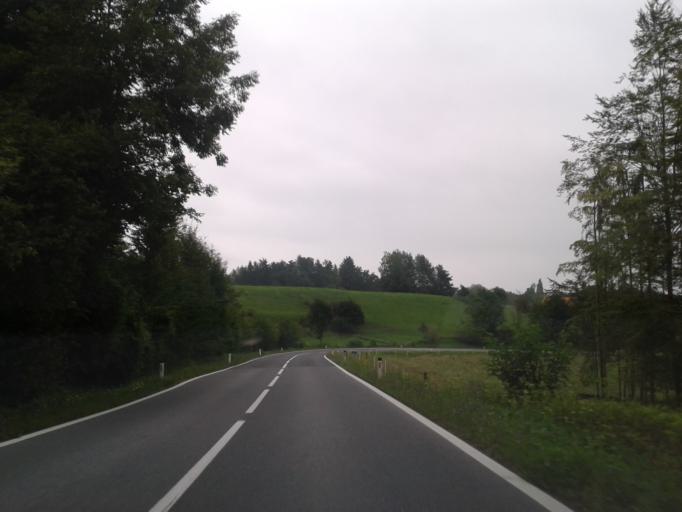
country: AT
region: Styria
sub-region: Politischer Bezirk Graz-Umgebung
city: Eggersdorf bei Graz
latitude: 47.1020
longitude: 15.5713
